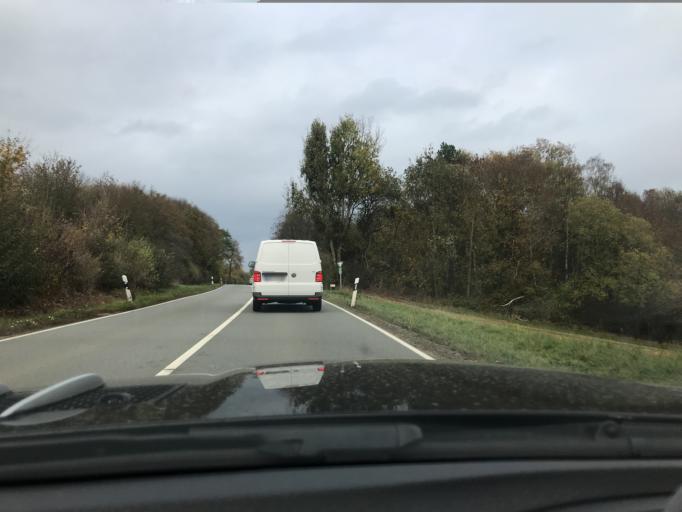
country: DE
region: Hesse
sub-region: Regierungsbezirk Kassel
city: Immenhausen
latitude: 51.4295
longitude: 9.4507
